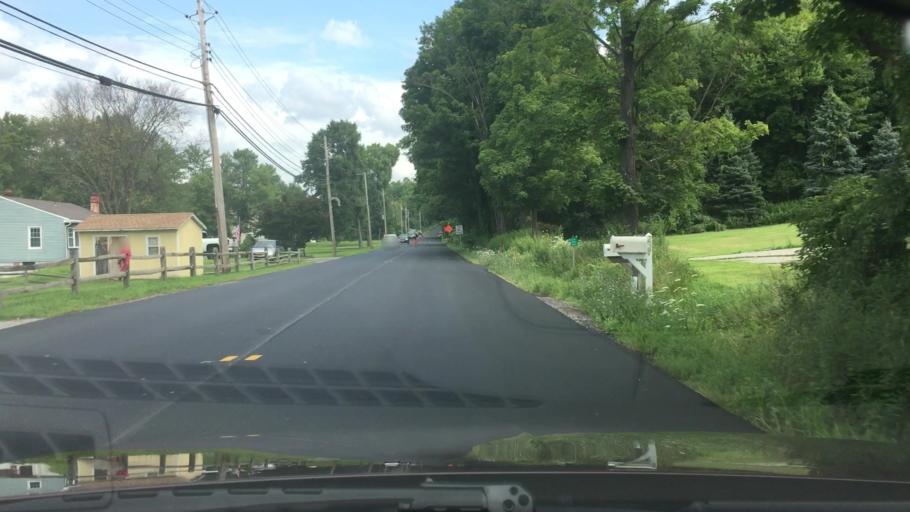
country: US
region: New York
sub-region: Dutchess County
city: Hillside Lake
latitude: 41.5746
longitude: -73.7468
